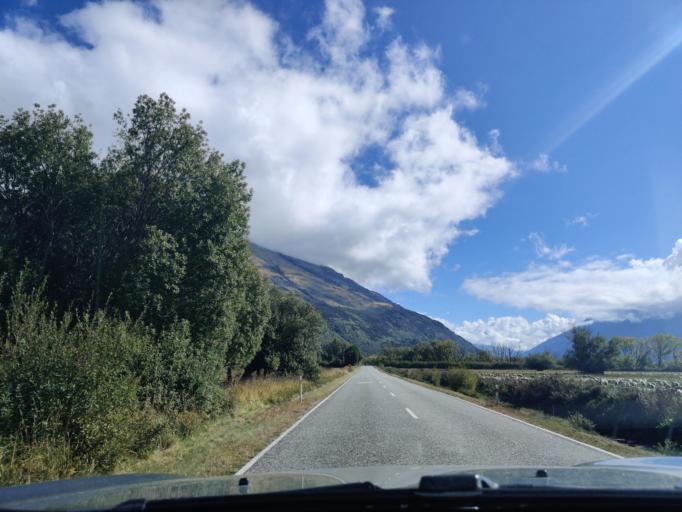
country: NZ
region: Otago
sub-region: Queenstown-Lakes District
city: Queenstown
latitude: -44.7909
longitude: 168.3999
